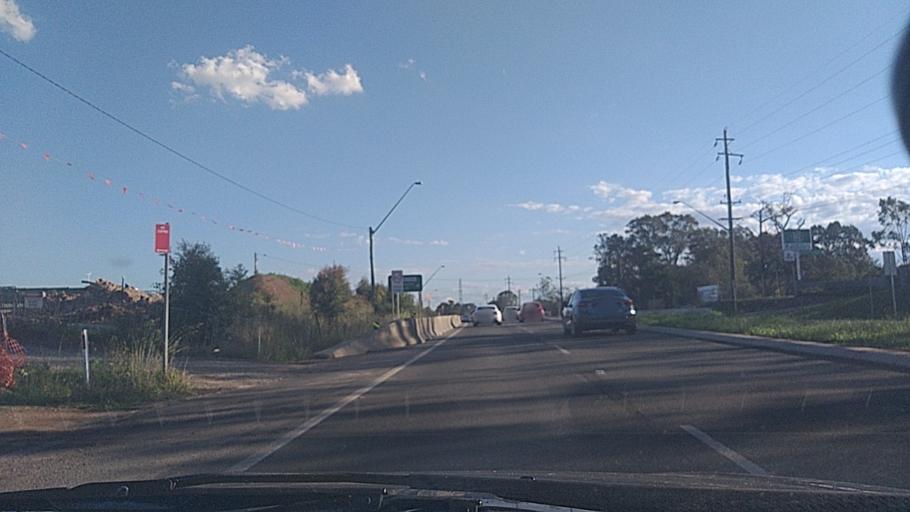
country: AU
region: New South Wales
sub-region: Penrith Municipality
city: Kingswood Park
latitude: -33.7915
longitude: 150.6996
